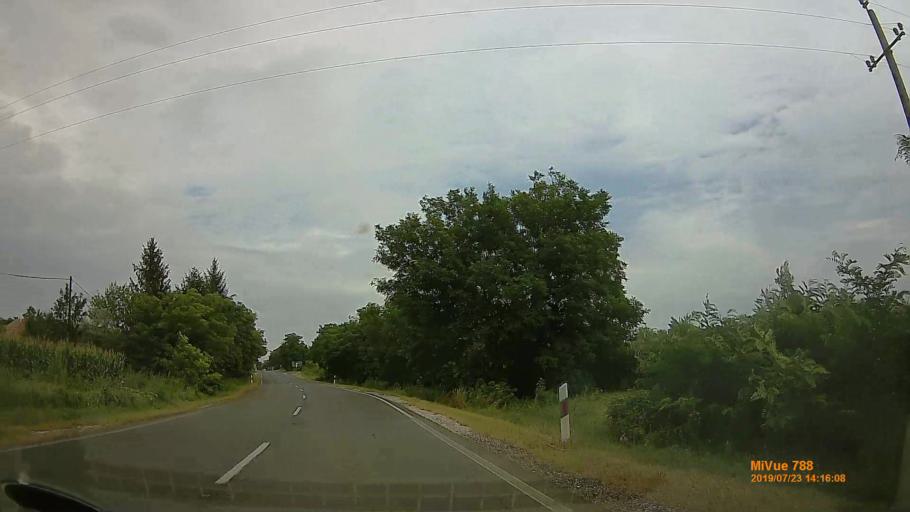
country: HU
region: Szabolcs-Szatmar-Bereg
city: Nagycserkesz
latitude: 47.9602
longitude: 21.5273
